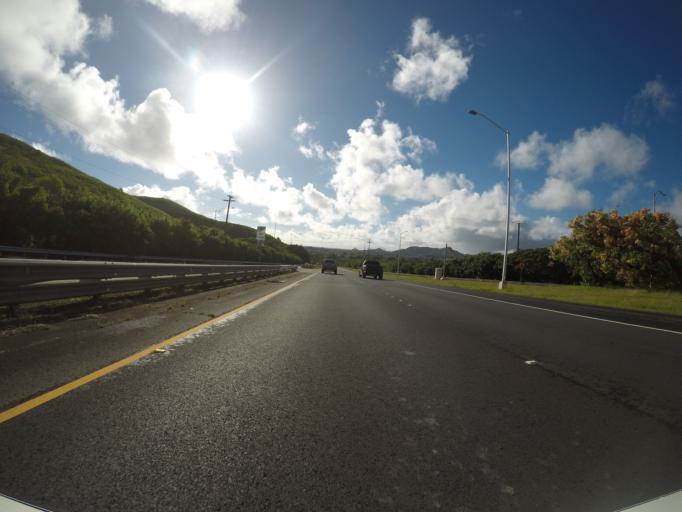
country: US
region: Hawaii
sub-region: Honolulu County
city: Kailua
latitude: 21.4063
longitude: -157.7650
